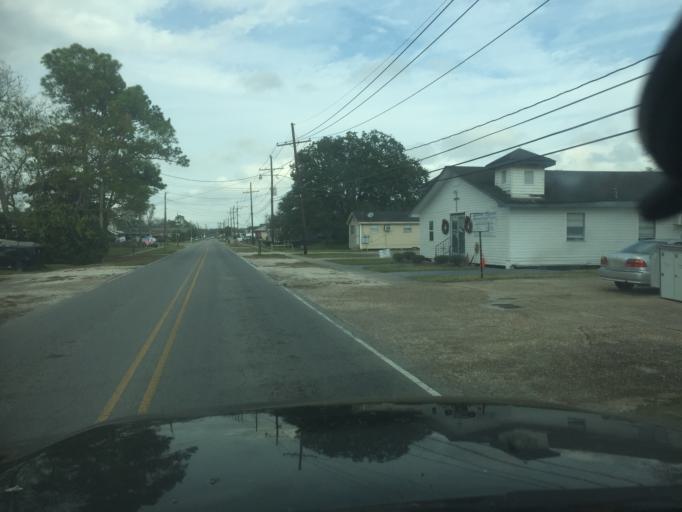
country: US
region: Louisiana
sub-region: Jefferson Parish
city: Waggaman
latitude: 29.9133
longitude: -90.2102
